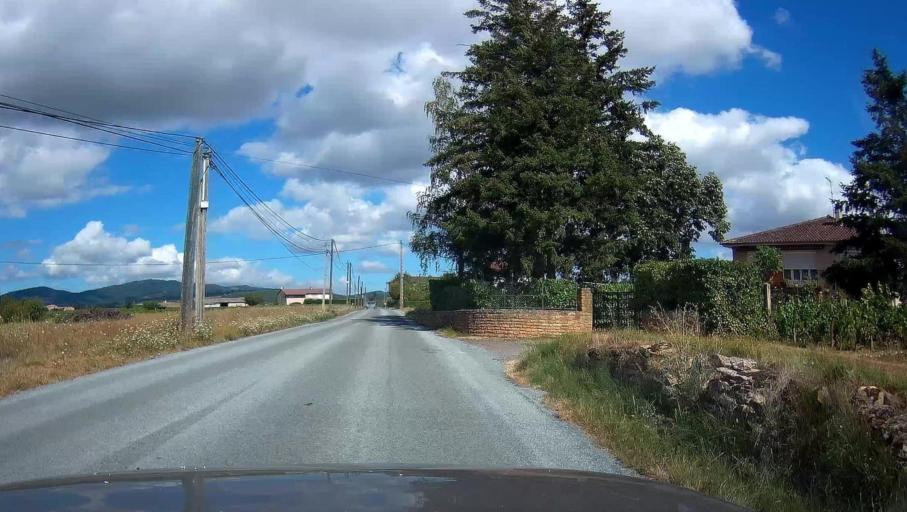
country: FR
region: Rhone-Alpes
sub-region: Departement du Rhone
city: Liergues
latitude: 45.9727
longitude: 4.6545
